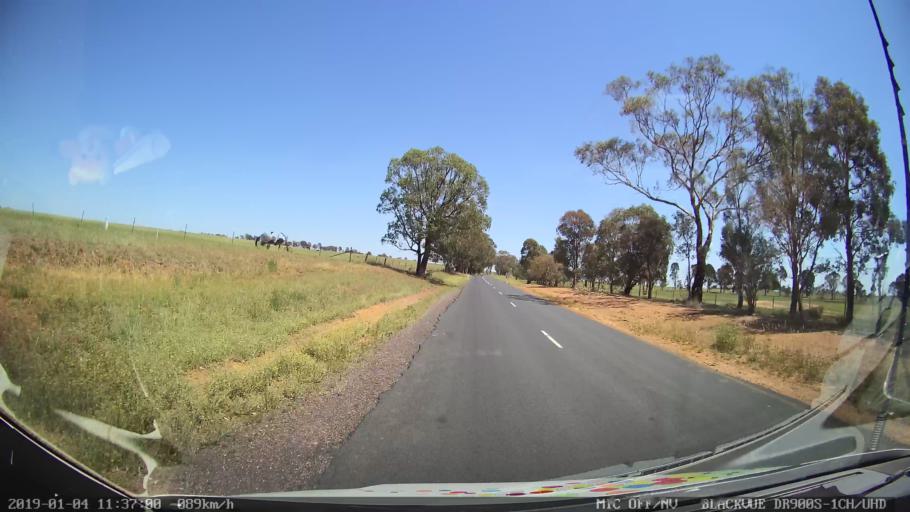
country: AU
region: New South Wales
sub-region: Cabonne
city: Molong
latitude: -33.0375
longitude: 148.8106
